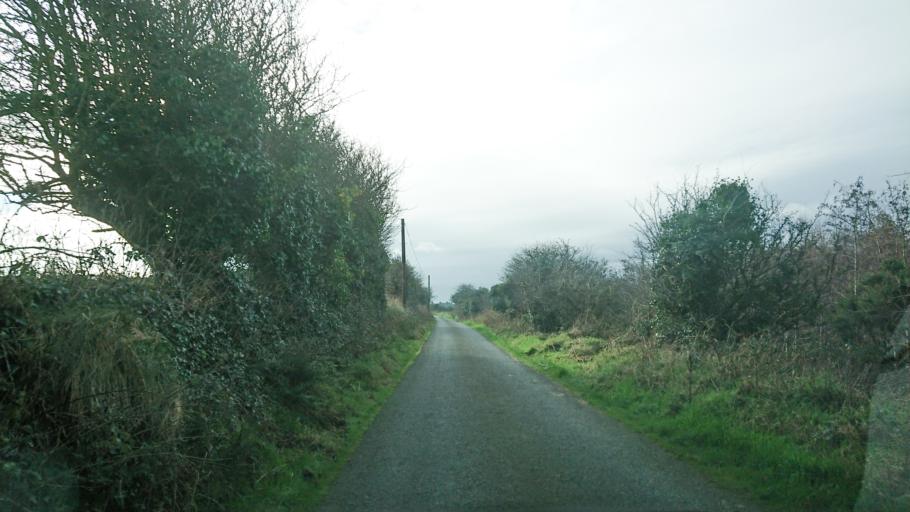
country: IE
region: Munster
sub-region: Waterford
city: Tra Mhor
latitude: 52.1527
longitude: -7.1917
